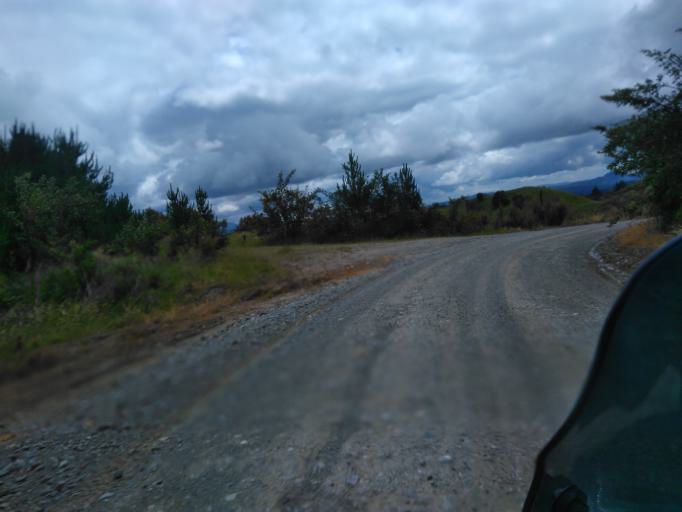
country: NZ
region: Gisborne
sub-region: Gisborne District
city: Gisborne
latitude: -38.1786
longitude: 178.1297
